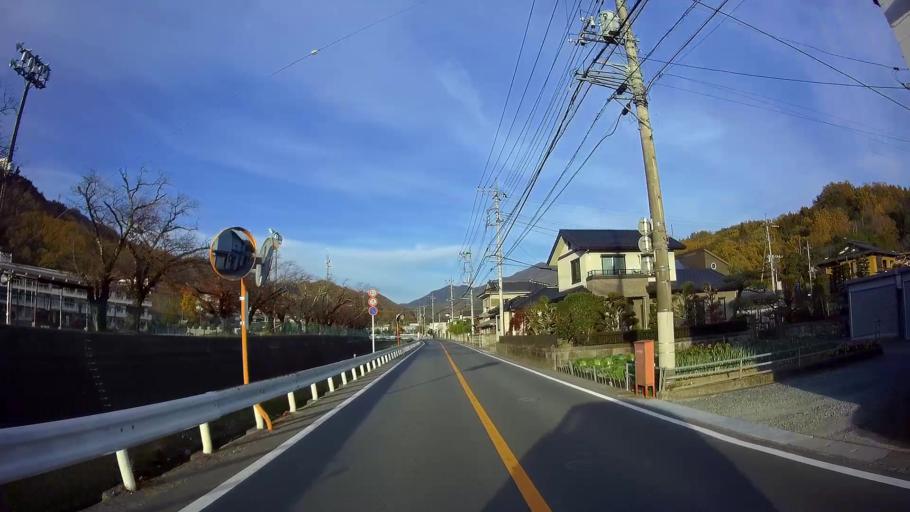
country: JP
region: Yamanashi
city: Ryuo
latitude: 35.4974
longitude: 138.4639
